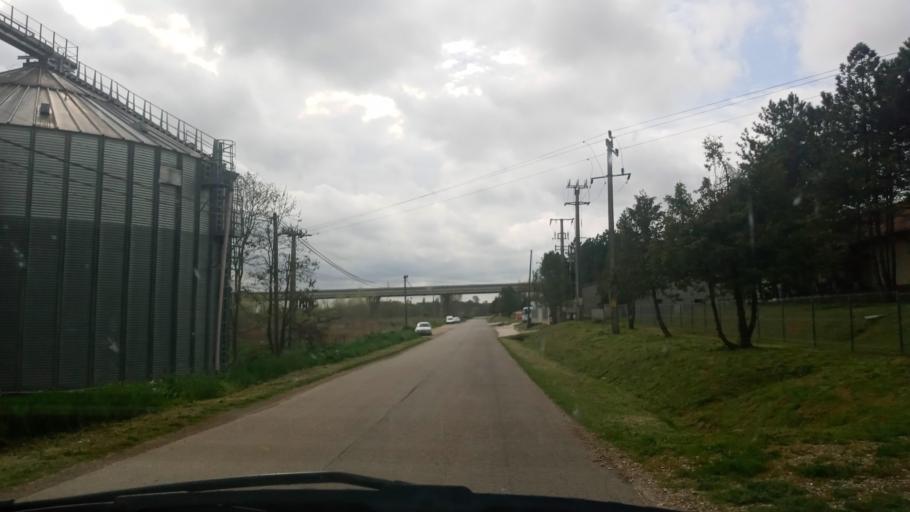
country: HU
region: Baranya
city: Boly
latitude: 45.9840
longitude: 18.4212
